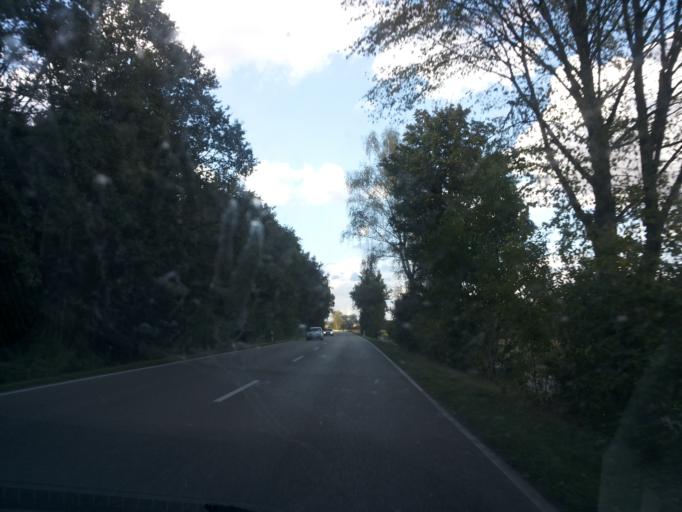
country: DE
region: Bavaria
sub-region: Upper Bavaria
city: Eitensheim
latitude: 48.7916
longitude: 11.3376
